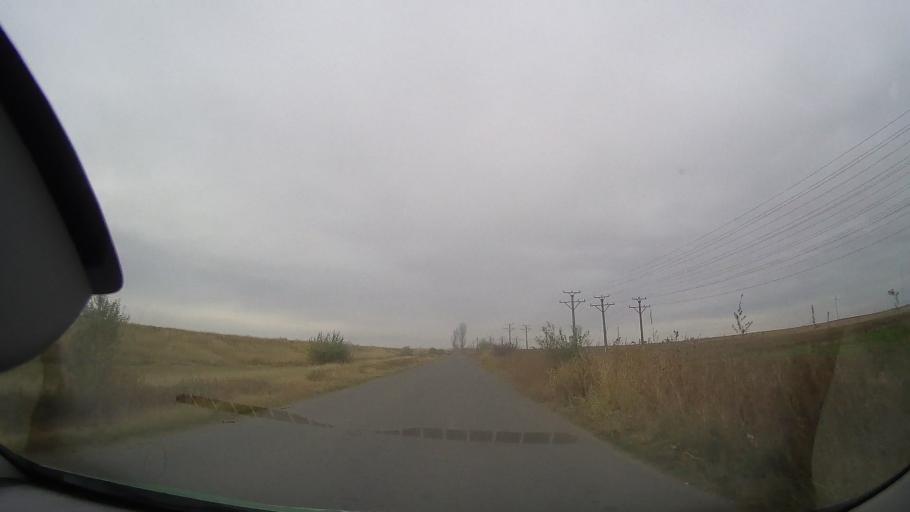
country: RO
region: Braila
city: Dudesti
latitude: 44.9027
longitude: 27.4321
